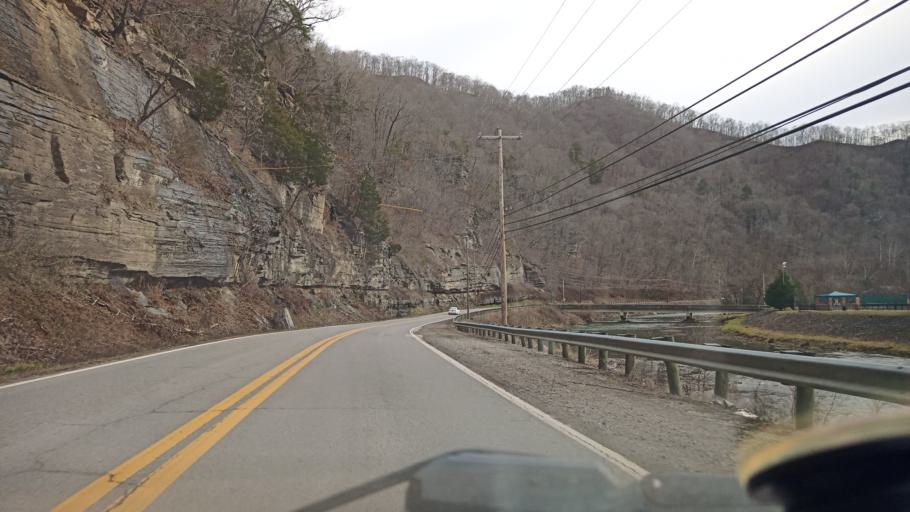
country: US
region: West Virginia
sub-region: Mingo County
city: Gilbert Creek
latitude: 37.6122
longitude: -81.8624
